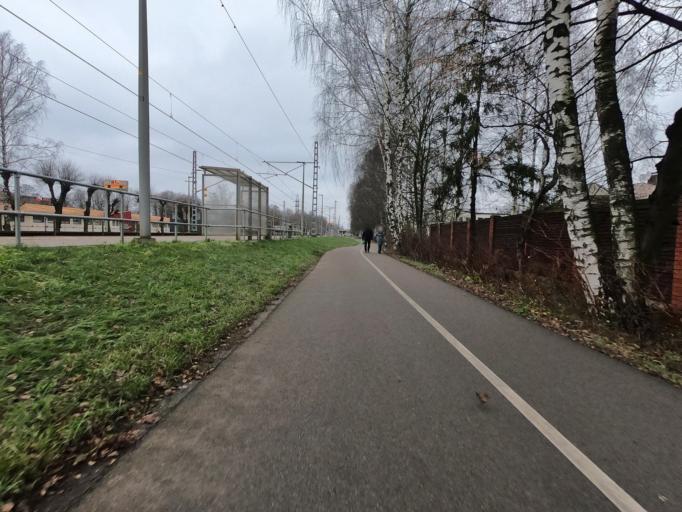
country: LV
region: Marupe
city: Marupe
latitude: 56.9504
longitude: 24.0019
